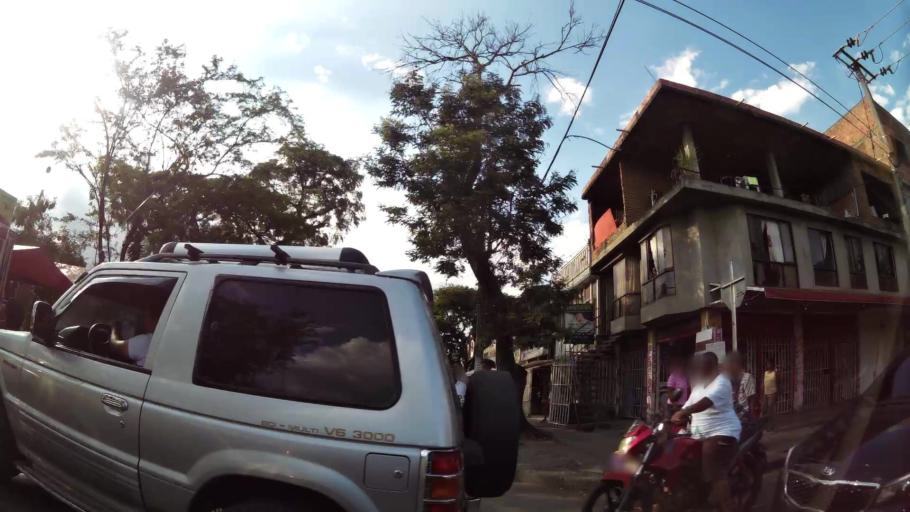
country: CO
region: Valle del Cauca
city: Cali
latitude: 3.4006
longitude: -76.5096
